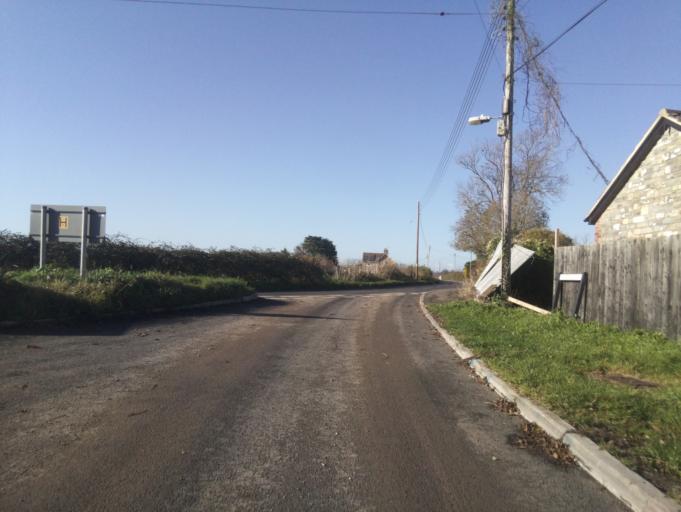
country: GB
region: England
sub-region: Somerset
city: Langport
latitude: 51.0349
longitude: -2.8050
